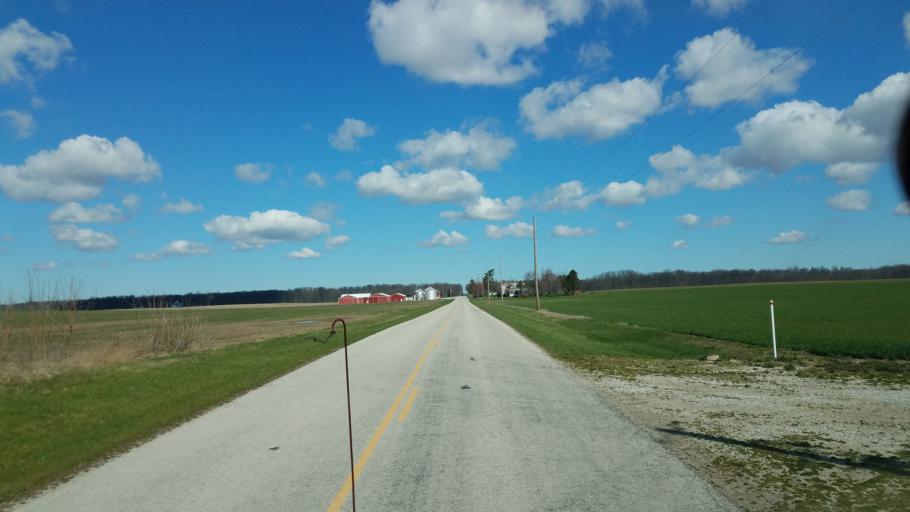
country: US
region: Ohio
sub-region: Sandusky County
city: Mount Carmel
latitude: 41.1724
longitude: -82.9382
